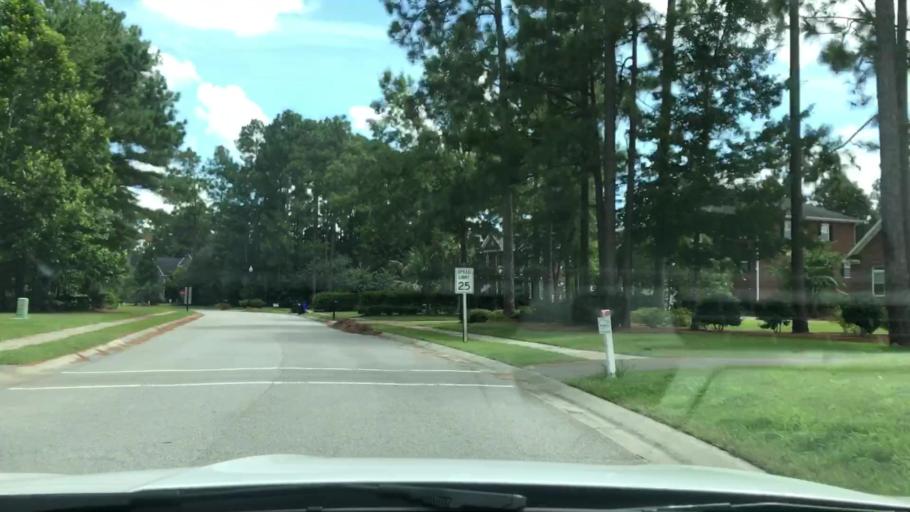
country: US
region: South Carolina
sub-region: Dorchester County
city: Summerville
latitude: 33.0343
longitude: -80.2223
